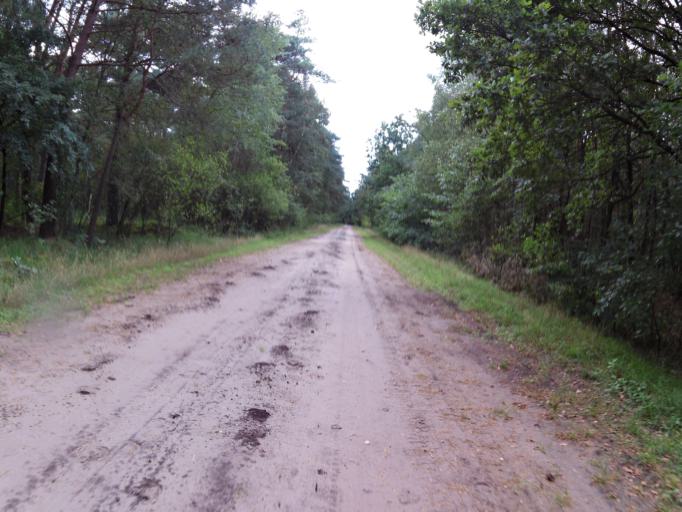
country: DE
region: Lower Saxony
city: Sandbostel
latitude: 53.3707
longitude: 9.1522
